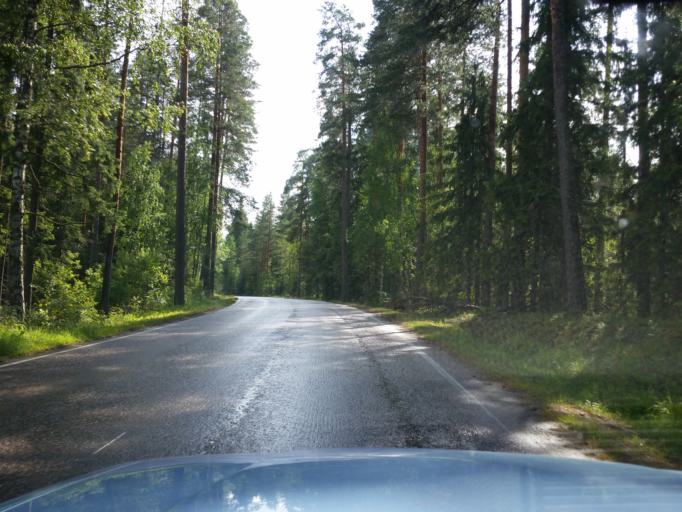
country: FI
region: Southern Savonia
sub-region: Savonlinna
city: Sulkava
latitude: 61.7989
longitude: 28.4127
